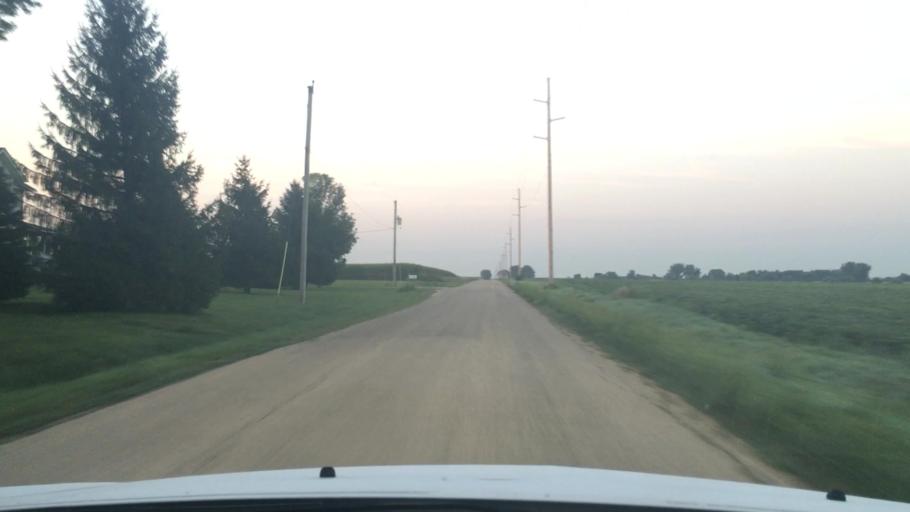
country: US
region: Illinois
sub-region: Ogle County
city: Rochelle
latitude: 41.8734
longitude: -89.0009
